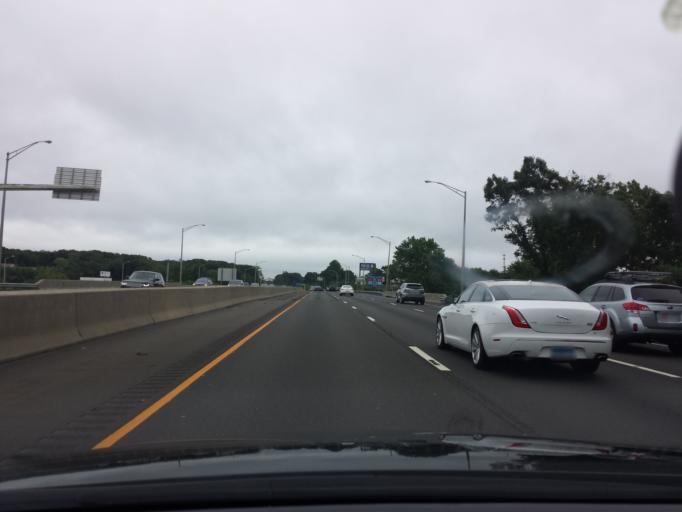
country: US
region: Connecticut
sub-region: New Haven County
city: Woodmont
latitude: 41.2379
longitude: -73.0235
